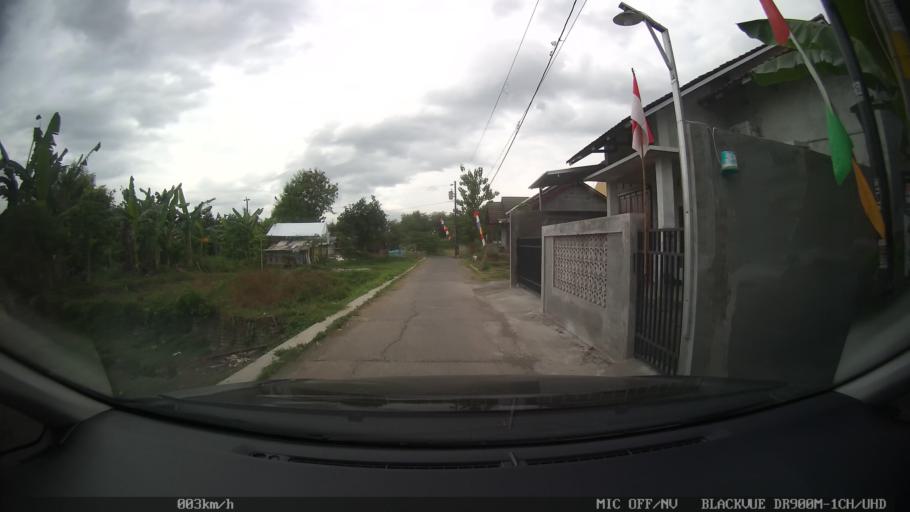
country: ID
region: Daerah Istimewa Yogyakarta
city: Depok
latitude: -7.8156
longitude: 110.4203
